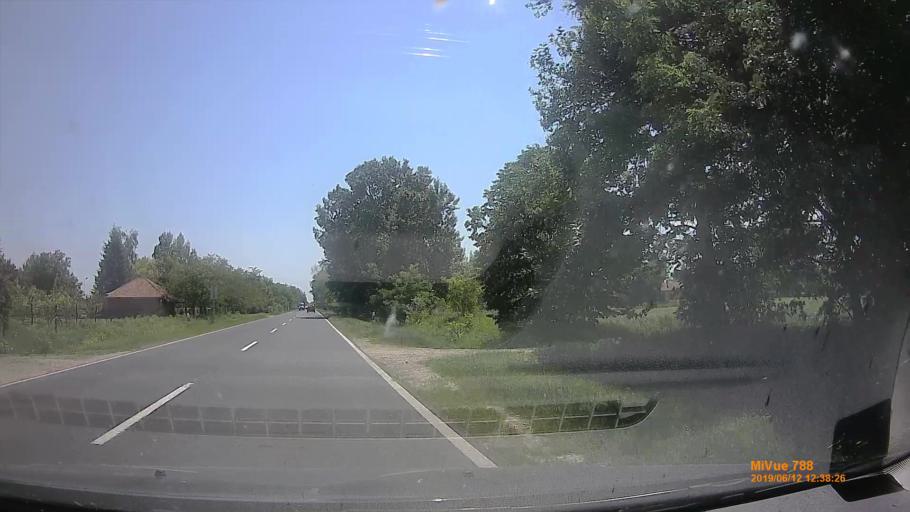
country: HU
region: Bacs-Kiskun
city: Varosfoeld
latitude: 46.7773
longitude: 19.8008
